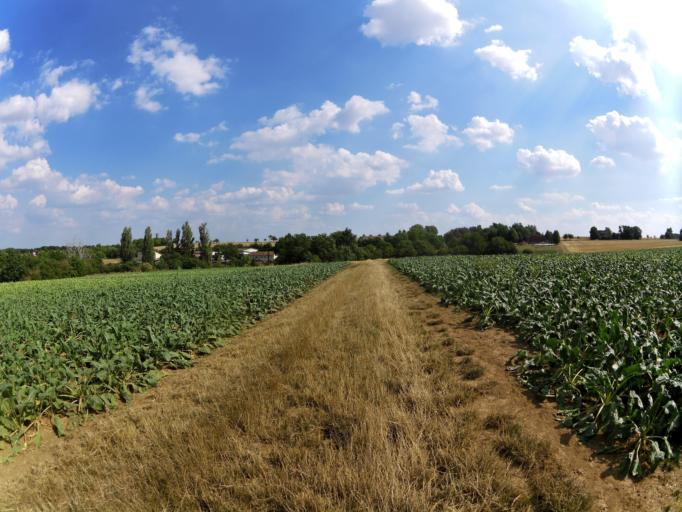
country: DE
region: Bavaria
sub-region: Regierungsbezirk Unterfranken
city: Ochsenfurt
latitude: 49.6535
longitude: 10.0698
